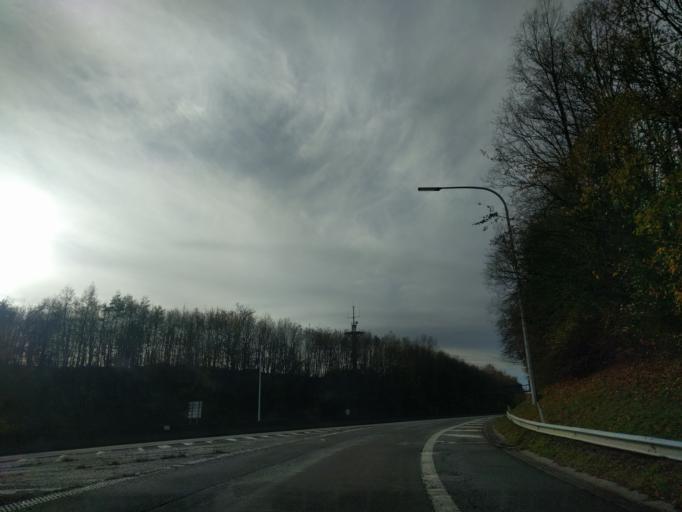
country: BE
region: Wallonia
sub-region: Province de Namur
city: Ciney
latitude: 50.2664
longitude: 5.0330
